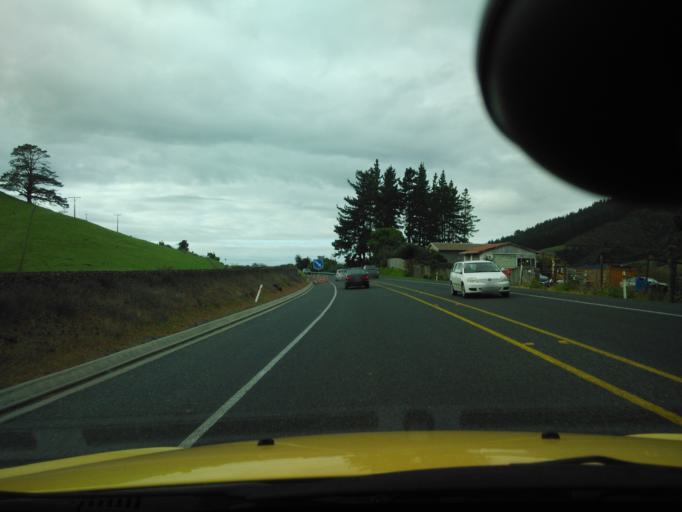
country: NZ
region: Waikato
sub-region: Waikato District
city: Ngaruawahia
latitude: -37.5986
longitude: 175.1640
